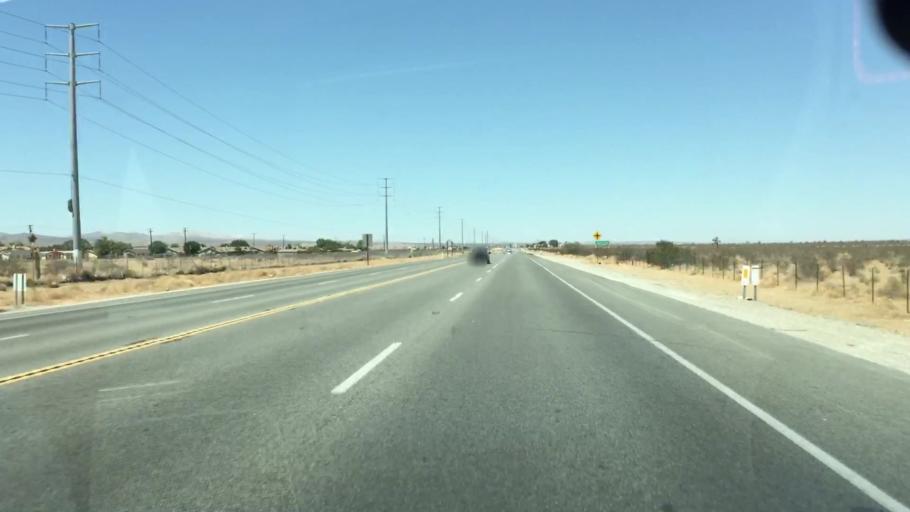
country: US
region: California
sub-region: San Bernardino County
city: Adelanto
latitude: 34.5902
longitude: -117.4157
